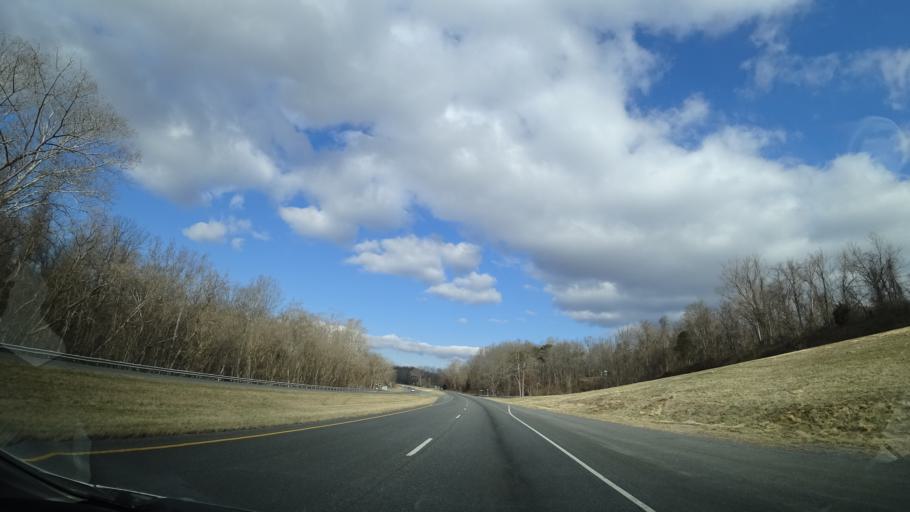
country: US
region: Virginia
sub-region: Warren County
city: Shenandoah Farms
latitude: 39.0439
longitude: -78.0019
